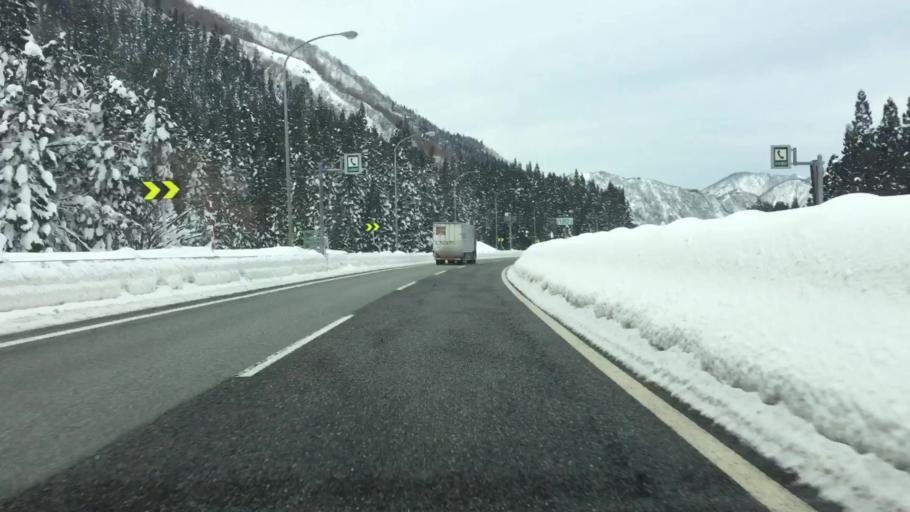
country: JP
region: Niigata
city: Shiozawa
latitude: 36.8867
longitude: 138.8497
